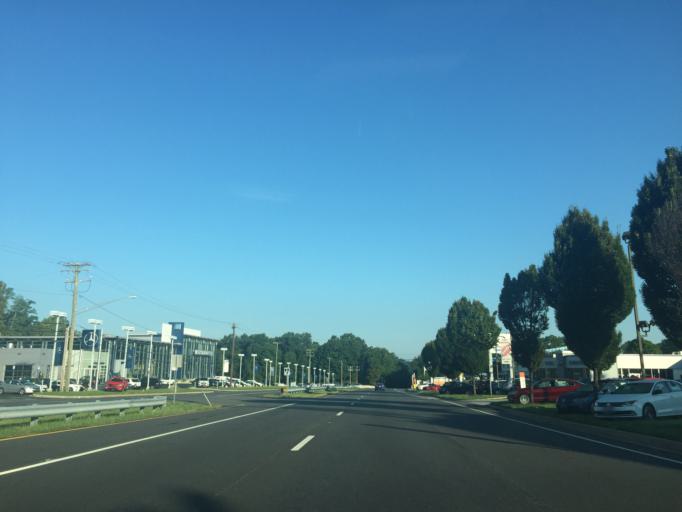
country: US
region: Maryland
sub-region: Howard County
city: Ellicott City
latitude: 39.2880
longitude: -76.7680
